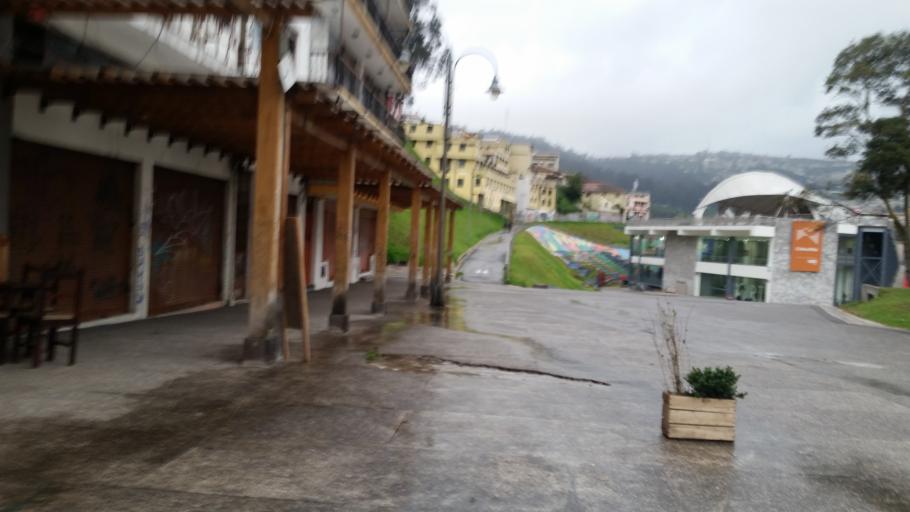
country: EC
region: Pichincha
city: Quito
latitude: -0.2267
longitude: -78.5123
